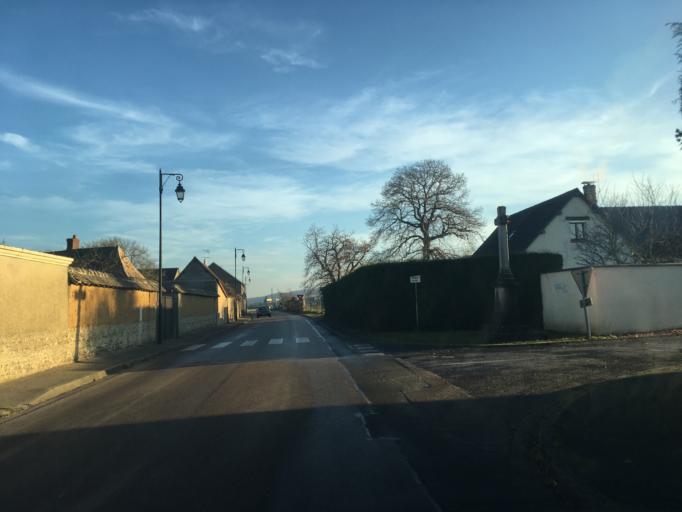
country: FR
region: Haute-Normandie
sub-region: Departement de l'Eure
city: Menilles
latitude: 49.0464
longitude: 1.3070
